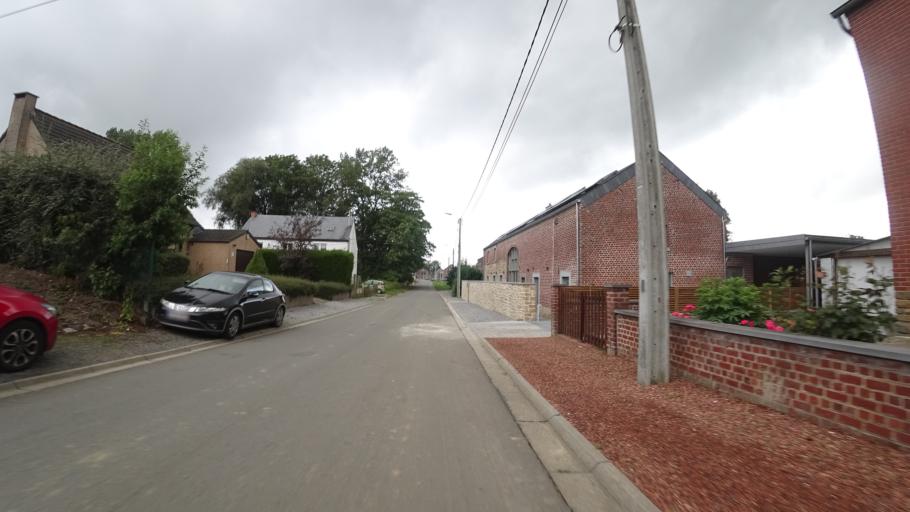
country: BE
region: Wallonia
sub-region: Province du Brabant Wallon
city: Perwez
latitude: 50.5311
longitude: 4.7912
